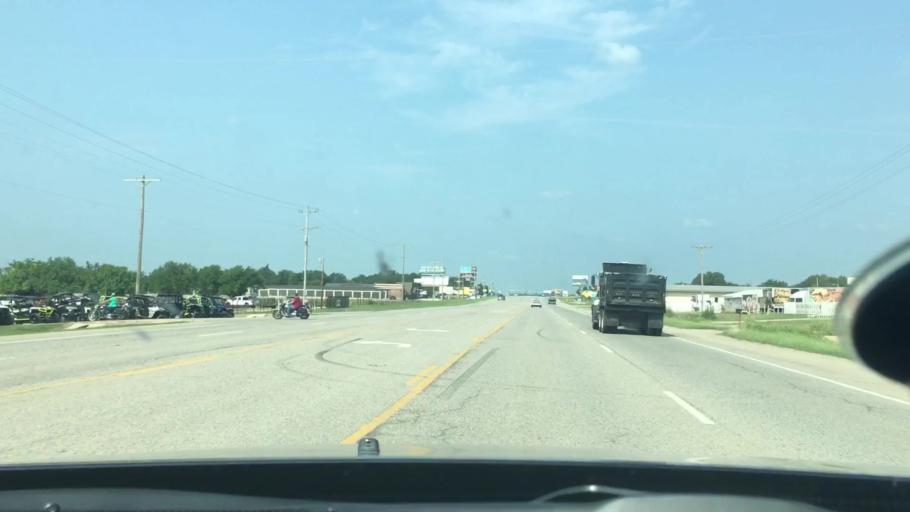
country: US
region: Oklahoma
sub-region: Bryan County
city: Calera
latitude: 33.9980
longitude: -96.4572
